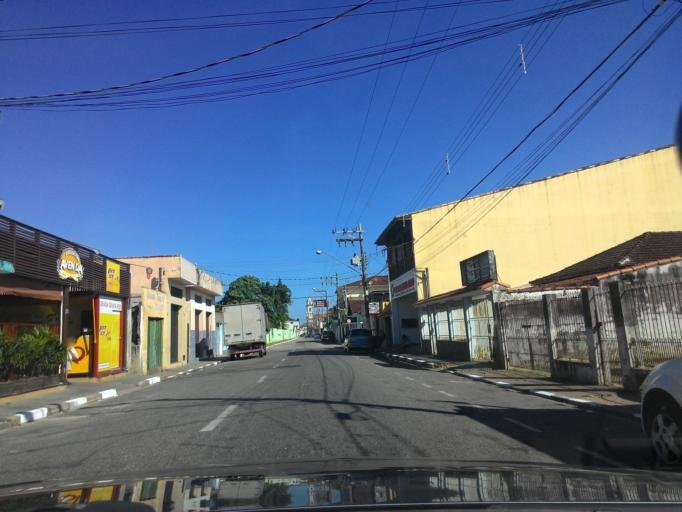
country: BR
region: Sao Paulo
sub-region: Iguape
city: Iguape
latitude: -24.7053
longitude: -47.5588
